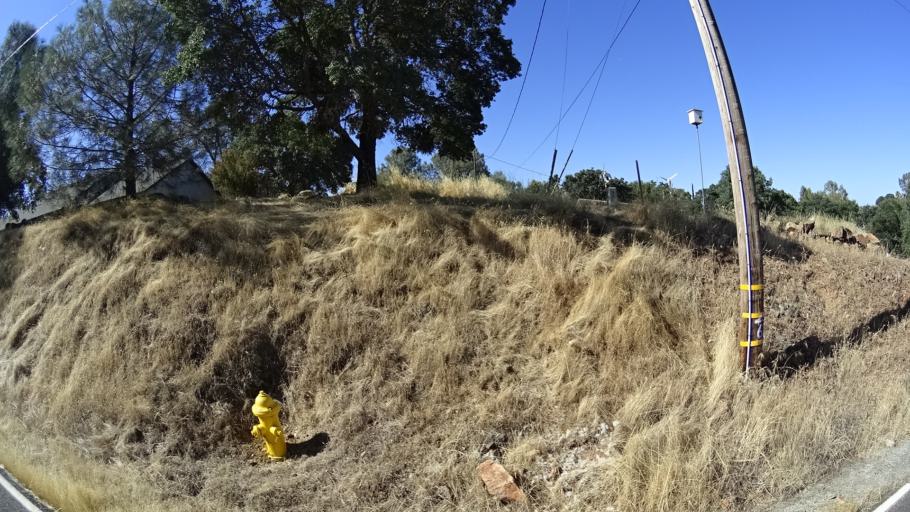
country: US
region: California
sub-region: Calaveras County
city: Rancho Calaveras
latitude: 38.1048
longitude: -120.8647
